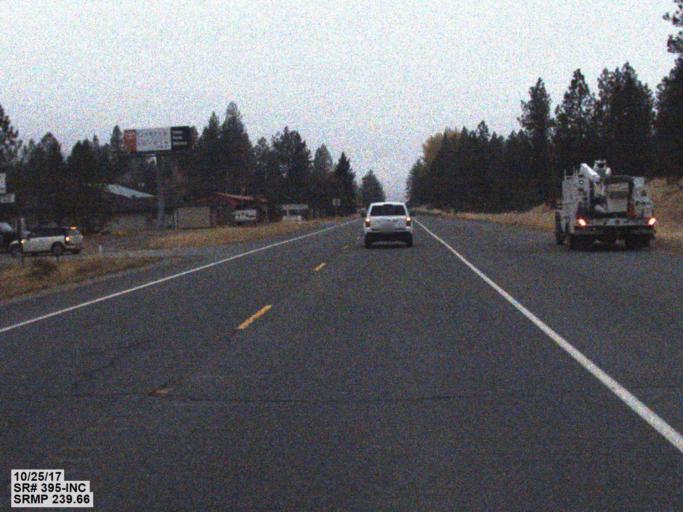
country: US
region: Washington
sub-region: Stevens County
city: Kettle Falls
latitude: 48.6083
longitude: -118.0853
